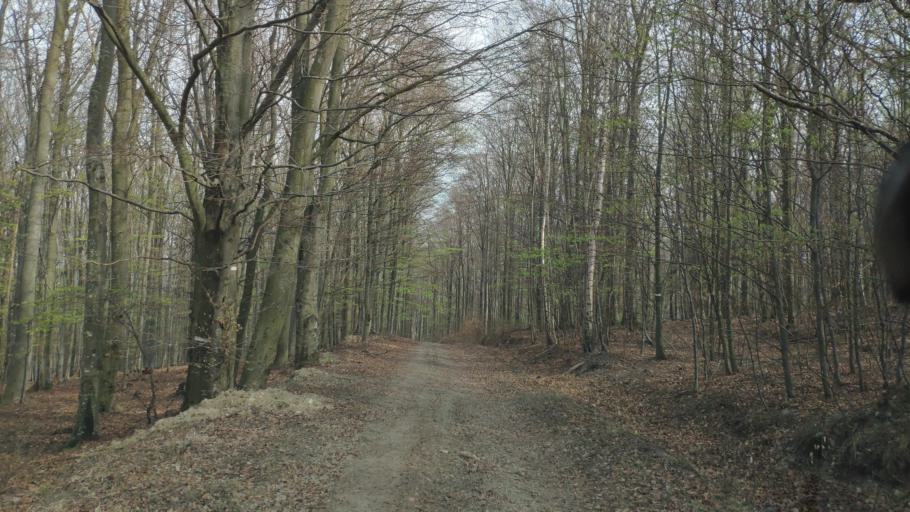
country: SK
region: Kosicky
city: Moldava nad Bodvou
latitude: 48.7349
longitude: 21.0595
